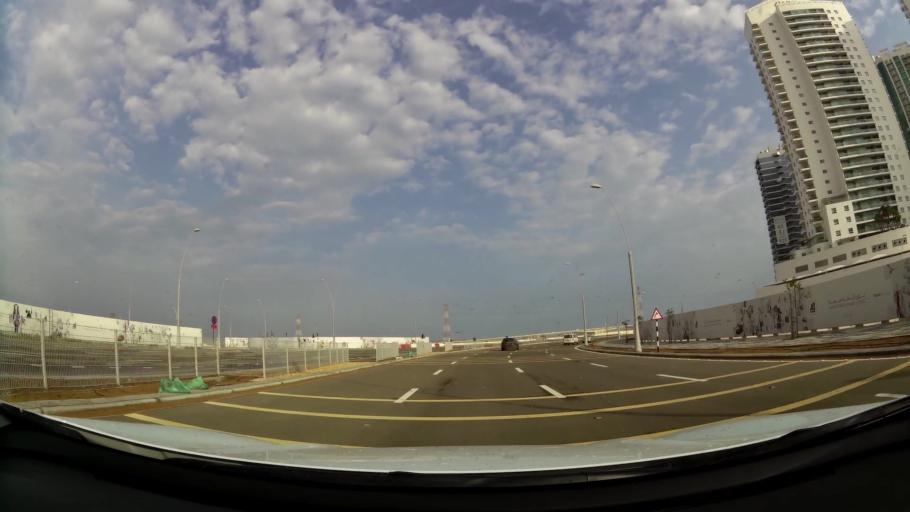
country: AE
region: Abu Dhabi
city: Abu Dhabi
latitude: 24.5099
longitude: 54.4049
